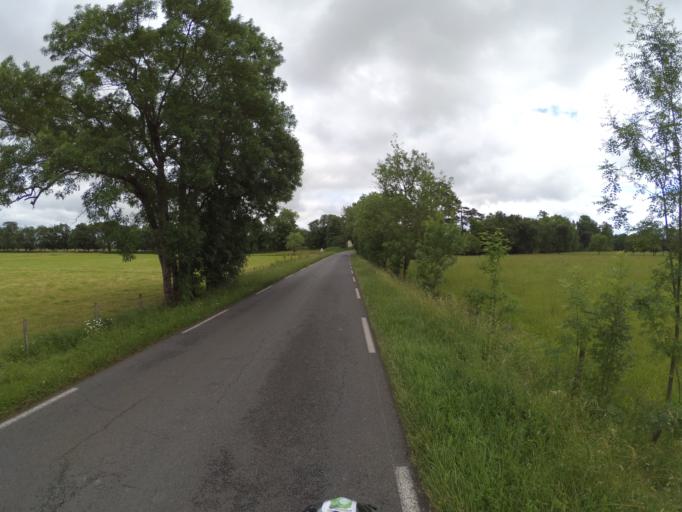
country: FR
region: Aquitaine
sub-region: Departement de la Gironde
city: Macau
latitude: 45.0169
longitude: -0.6204
